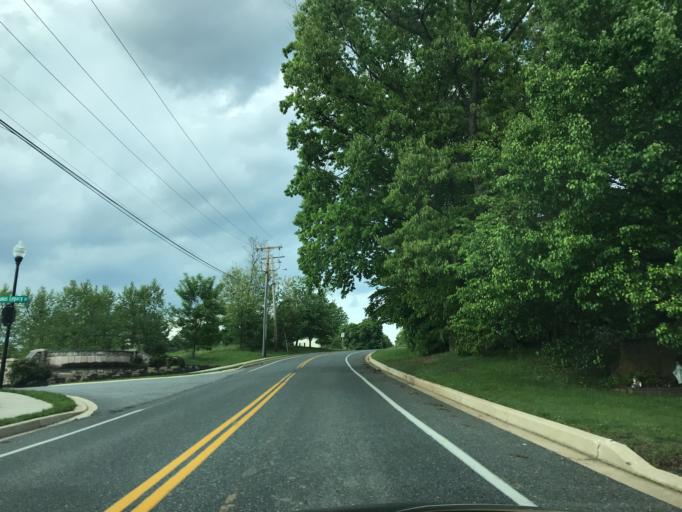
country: US
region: Maryland
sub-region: Harford County
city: Bel Air North
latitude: 39.5512
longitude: -76.3785
